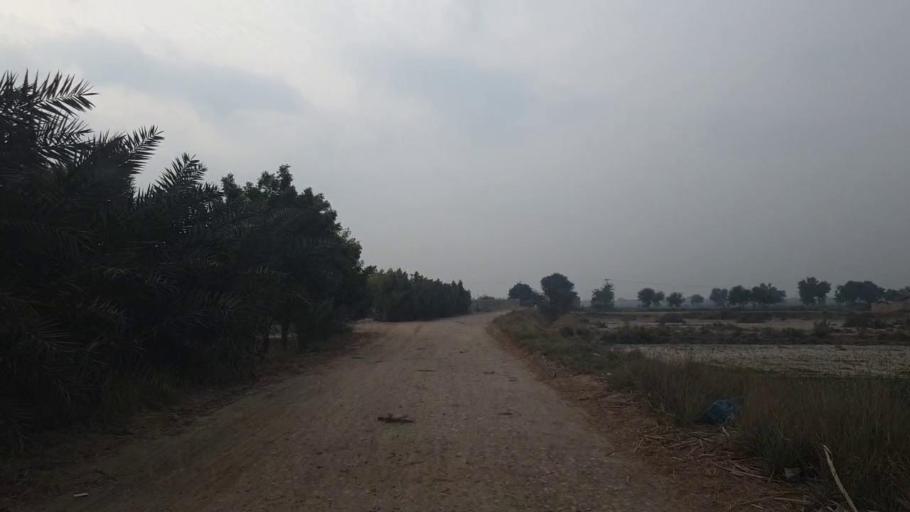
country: PK
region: Sindh
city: Tando Adam
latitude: 25.7379
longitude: 68.6824
